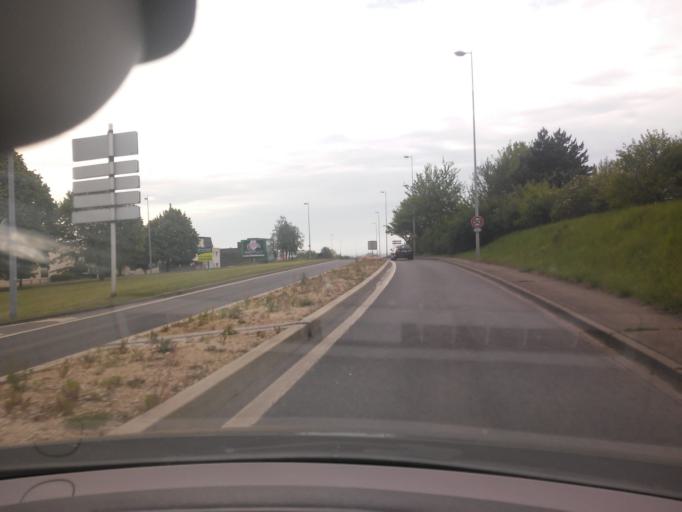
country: FR
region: Lorraine
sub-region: Departement de Meurthe-et-Moselle
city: Laxou
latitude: 48.6927
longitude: 6.1302
